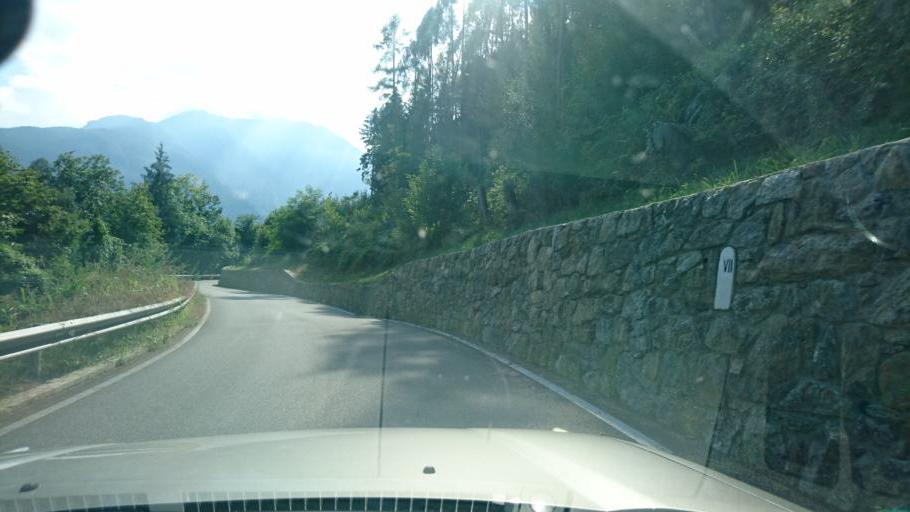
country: IT
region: Lombardy
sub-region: Provincia di Brescia
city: Berzo
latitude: 46.0954
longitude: 10.3098
